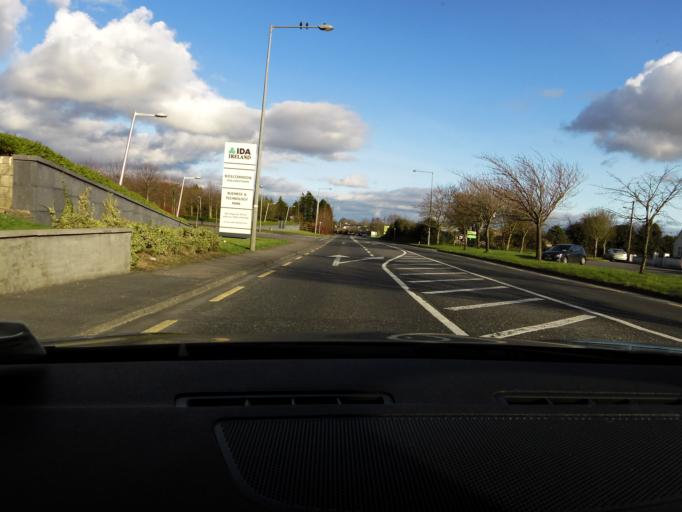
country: IE
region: Connaught
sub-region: Roscommon
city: Roscommon
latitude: 53.6404
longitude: -8.2057
